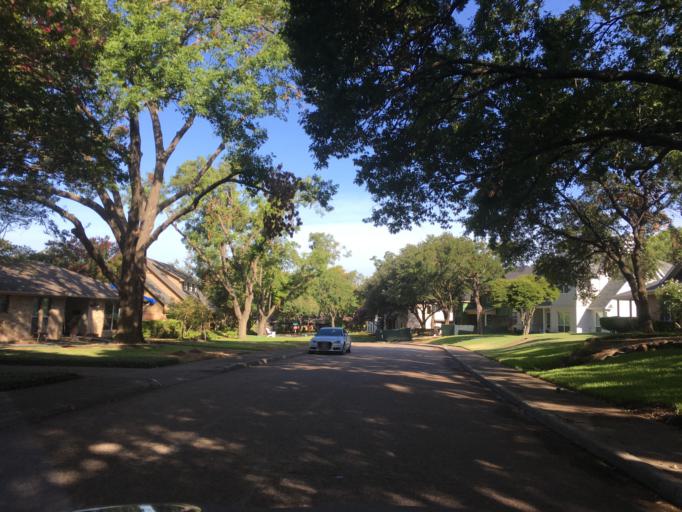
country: US
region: Texas
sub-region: Dallas County
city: Richardson
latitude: 32.8822
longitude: -96.7278
